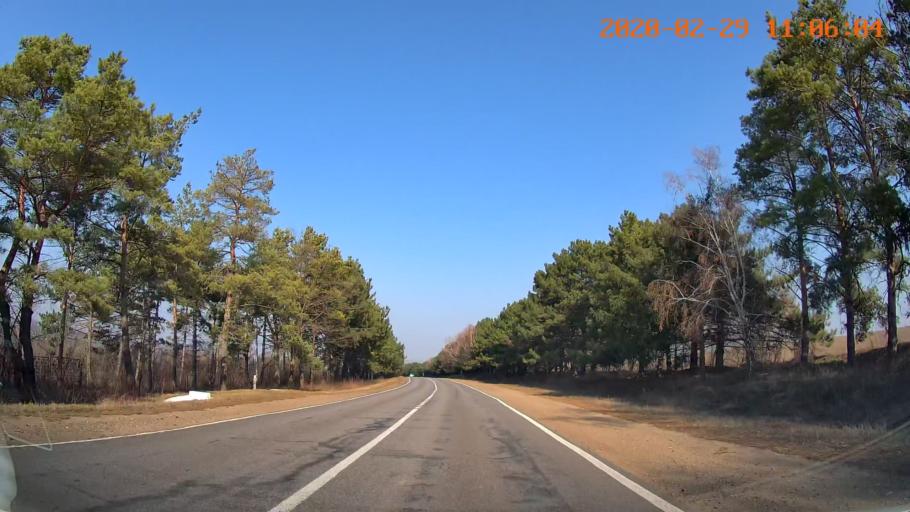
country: MD
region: Criuleni
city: Criuleni
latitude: 47.2100
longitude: 29.1897
